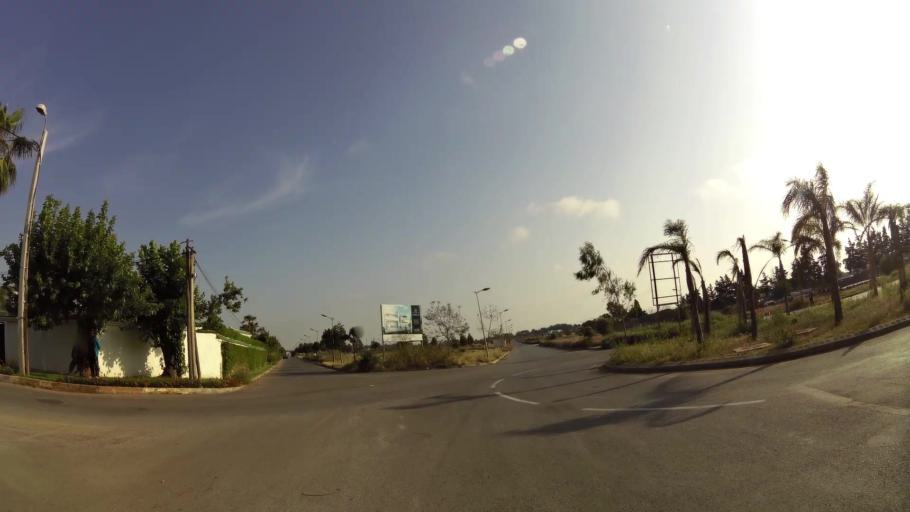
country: MA
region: Rabat-Sale-Zemmour-Zaer
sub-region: Rabat
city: Rabat
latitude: 33.9337
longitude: -6.8119
